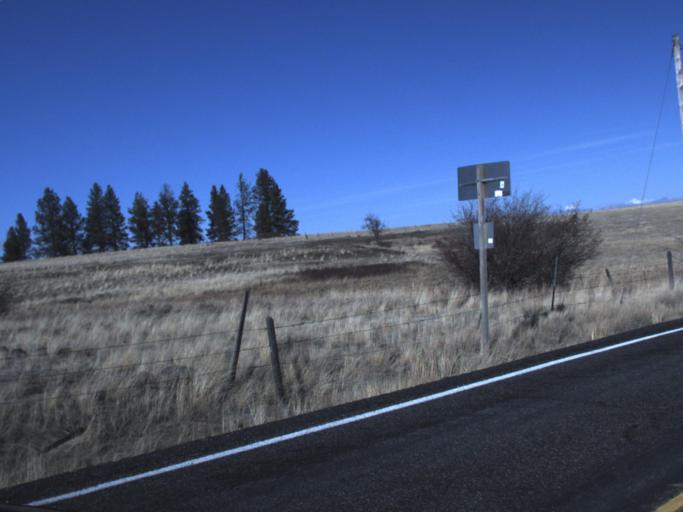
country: US
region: Washington
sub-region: Asotin County
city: Asotin
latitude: 46.1381
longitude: -117.1306
